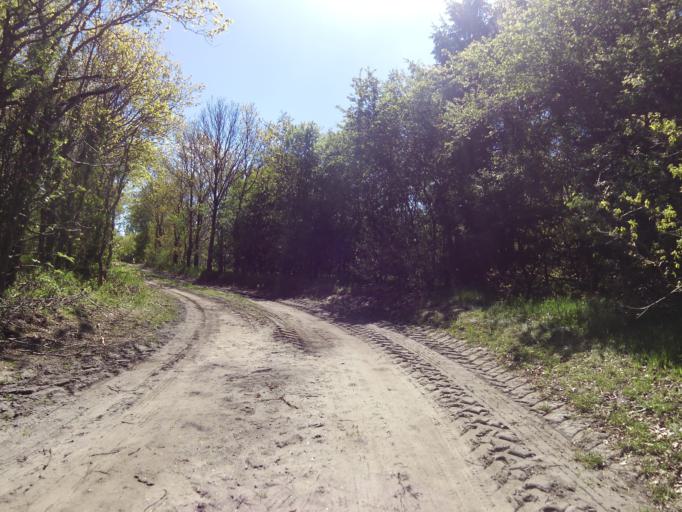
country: DK
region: South Denmark
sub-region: Tonder Kommune
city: Sherrebek
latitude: 55.2322
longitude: 8.7327
